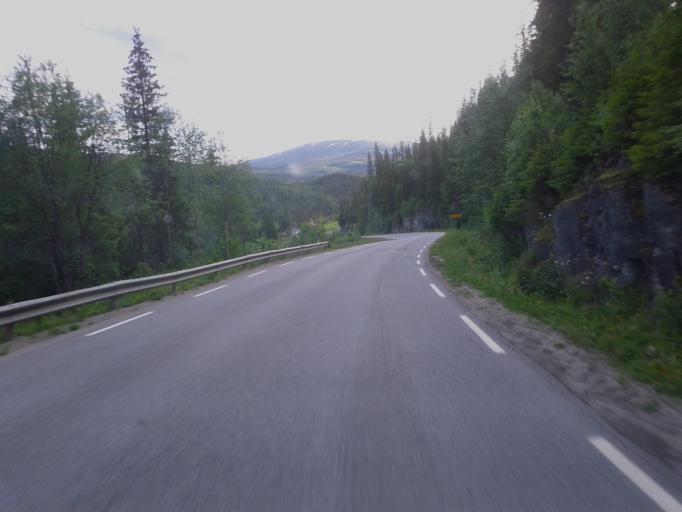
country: NO
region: Nordland
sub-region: Grane
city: Trofors
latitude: 65.5196
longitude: 13.6311
